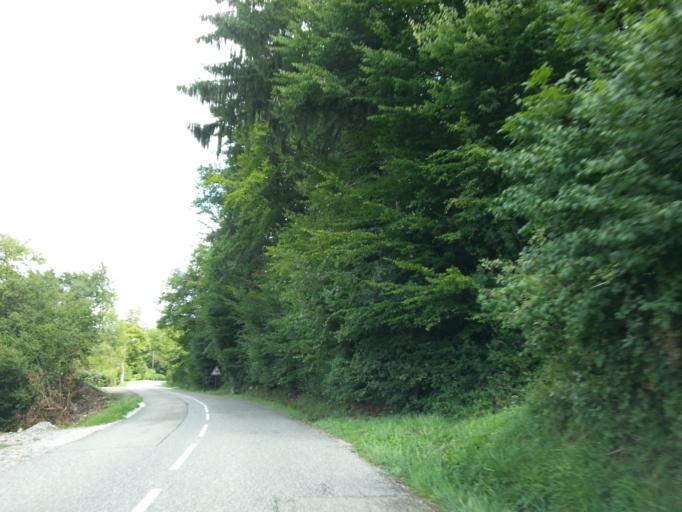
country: FR
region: Rhone-Alpes
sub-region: Departement de la Haute-Savoie
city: Menthon-Saint-Bernard
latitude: 45.8635
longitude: 6.2178
